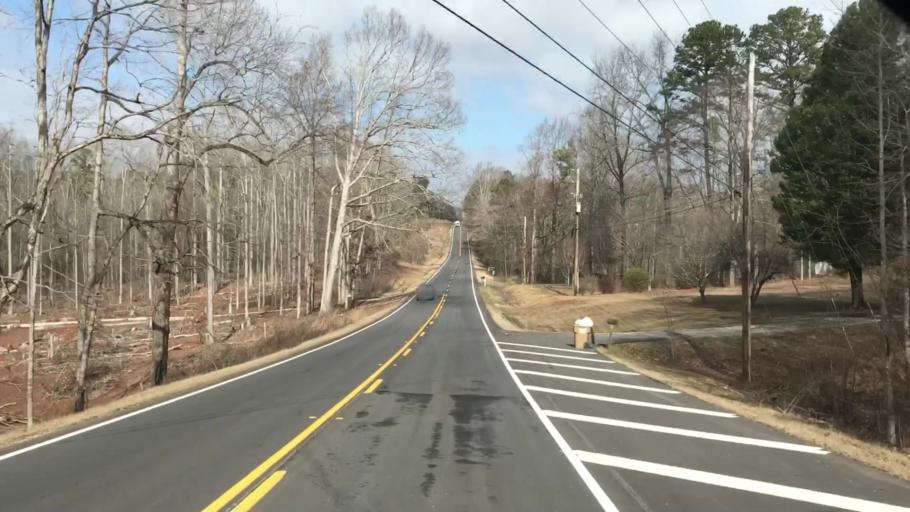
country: US
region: Georgia
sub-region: Jackson County
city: Braselton
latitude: 34.1478
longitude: -83.8376
